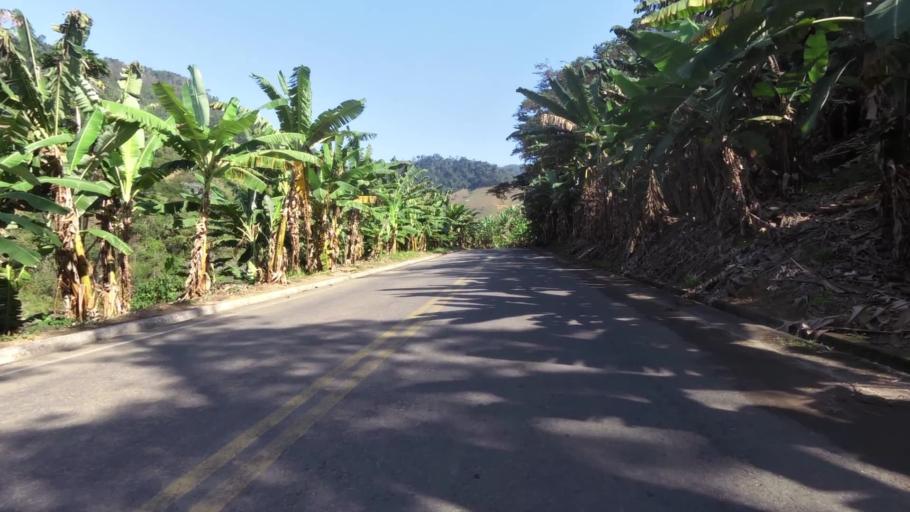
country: BR
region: Espirito Santo
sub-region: Alfredo Chaves
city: Alfredo Chaves
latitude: -20.6263
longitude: -40.7687
